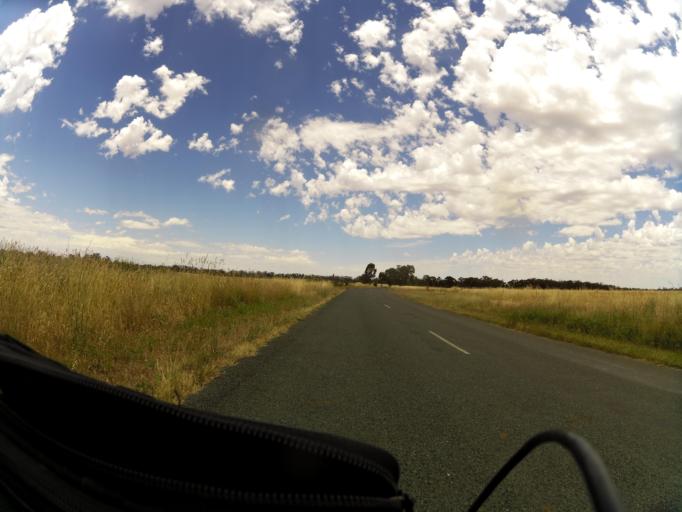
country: AU
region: Victoria
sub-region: Greater Shepparton
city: Shepparton
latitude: -36.6746
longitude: 145.1969
